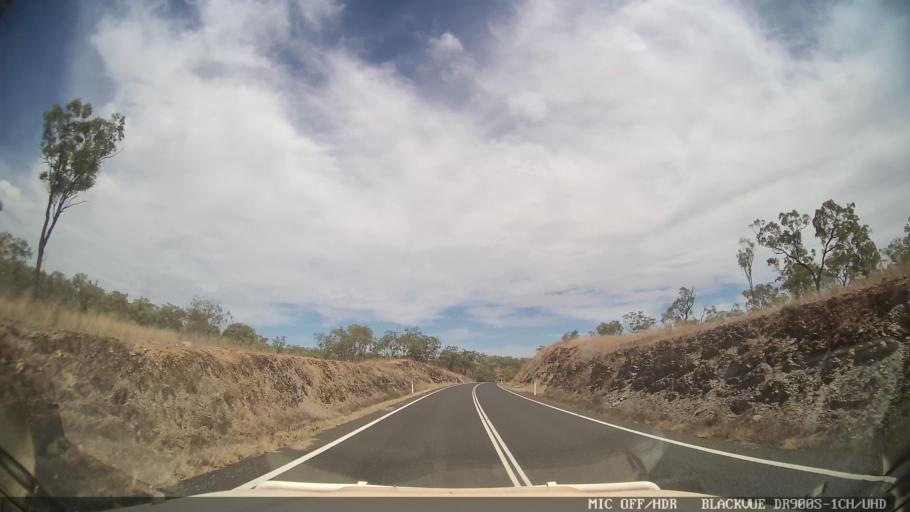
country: AU
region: Queensland
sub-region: Cairns
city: Port Douglas
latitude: -16.1488
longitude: 144.7666
